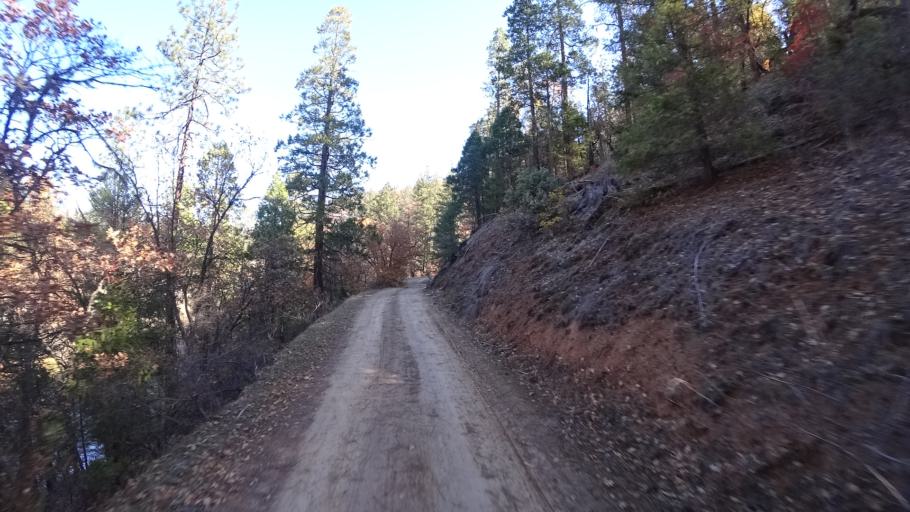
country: US
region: California
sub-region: Siskiyou County
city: Yreka
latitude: 41.8578
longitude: -122.7501
